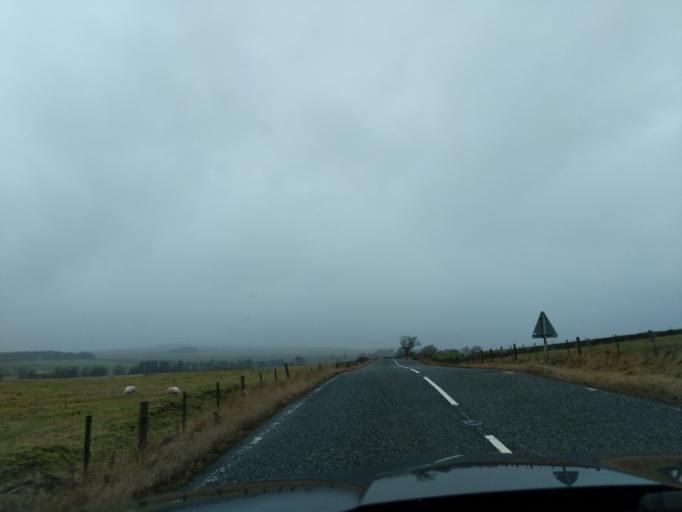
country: GB
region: England
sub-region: Northumberland
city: Otterburn
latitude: 55.2400
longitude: -2.2068
